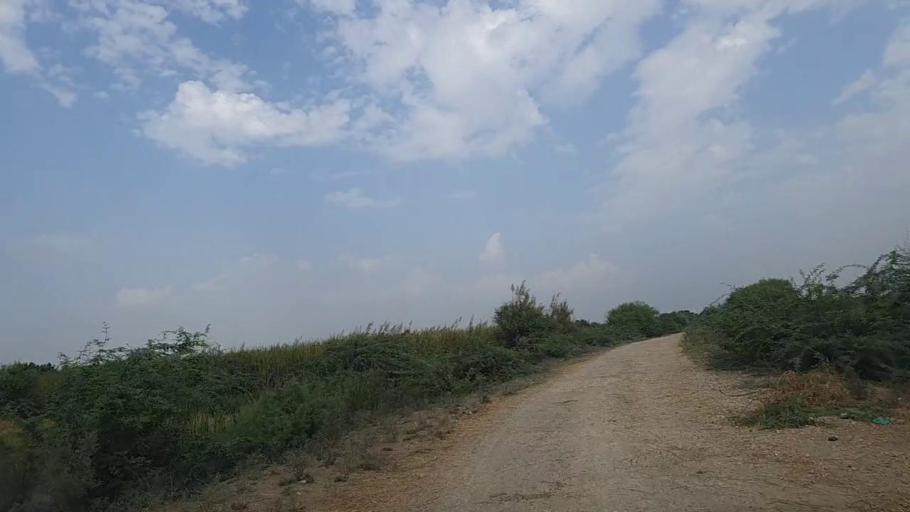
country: PK
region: Sindh
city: Daro Mehar
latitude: 24.7131
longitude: 68.1533
